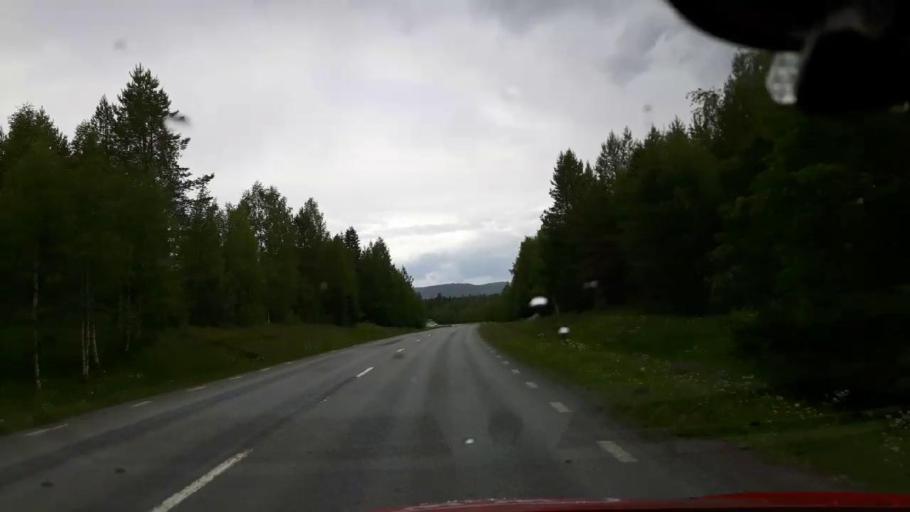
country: SE
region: Jaemtland
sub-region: Krokoms Kommun
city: Krokom
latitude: 63.4243
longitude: 14.2175
